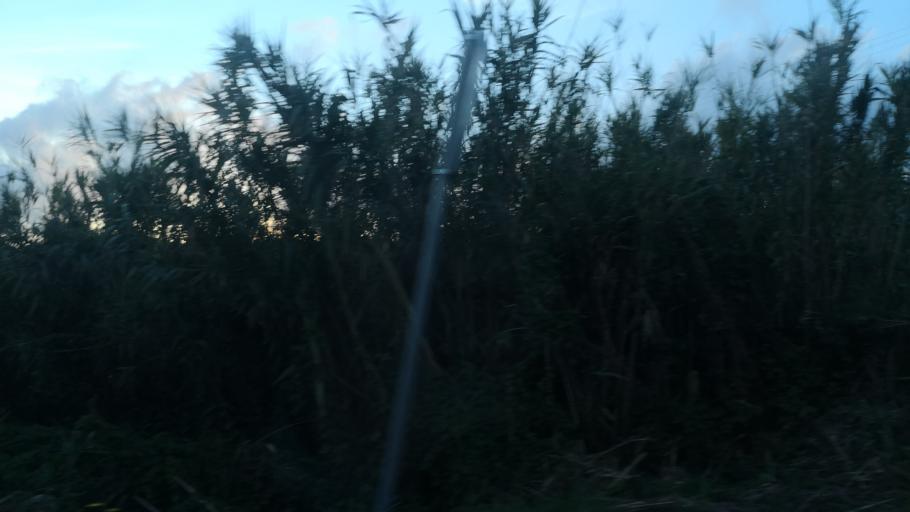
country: PT
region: Madeira
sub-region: Santa Cruz
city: Camacha
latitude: 32.6764
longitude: -16.8249
